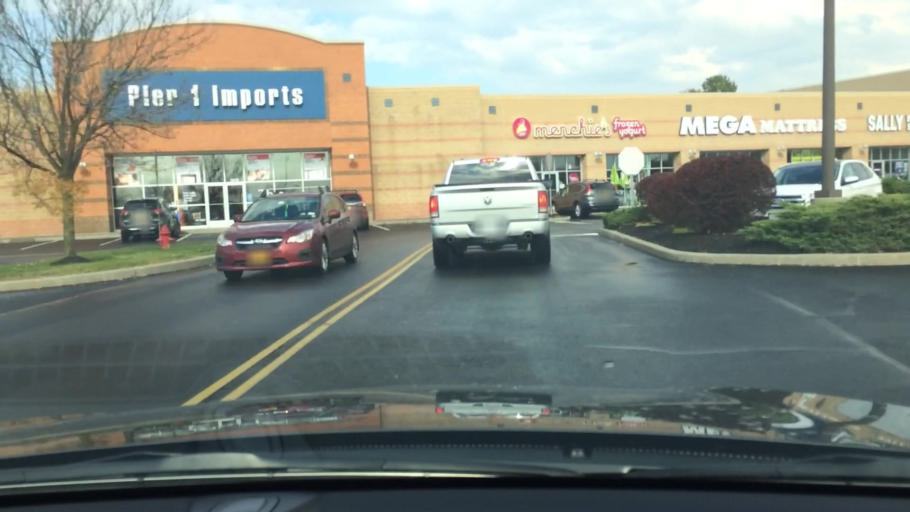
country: US
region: New York
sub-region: Saratoga County
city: Saratoga Springs
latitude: 43.1072
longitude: -73.7397
